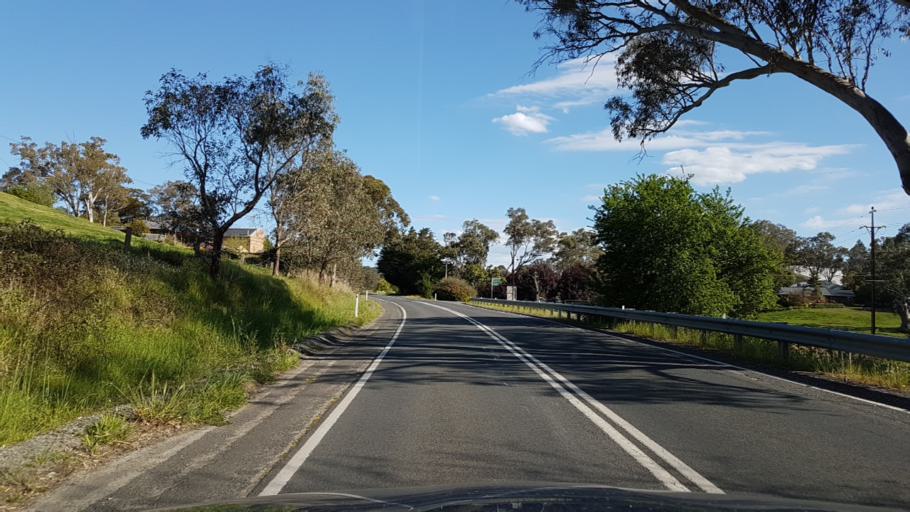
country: AU
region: South Australia
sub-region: Adelaide Hills
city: Gumeracha
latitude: -34.8481
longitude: 138.8926
